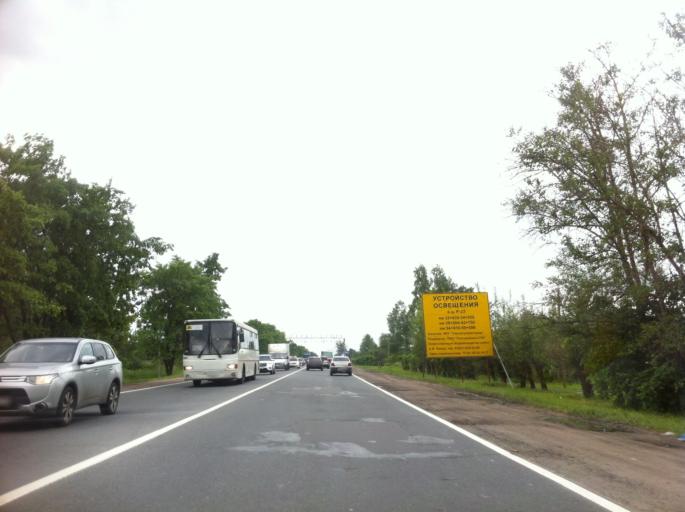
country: RU
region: Leningrad
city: Maloye Verevo
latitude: 59.6650
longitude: 30.2270
